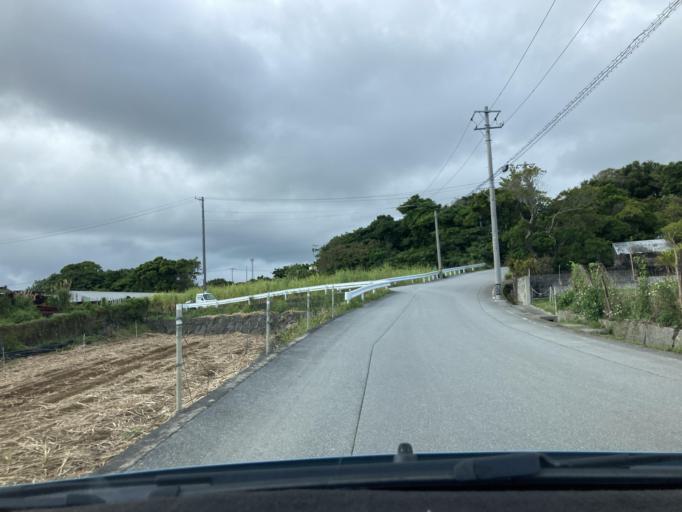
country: JP
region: Okinawa
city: Itoman
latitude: 26.1284
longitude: 127.6856
